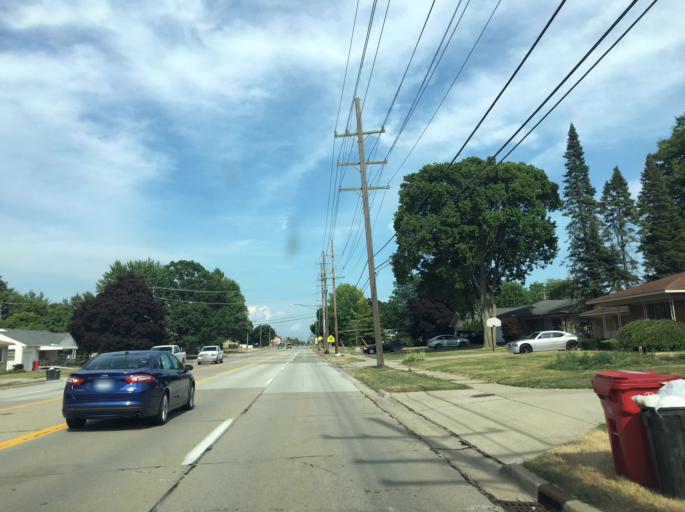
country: US
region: Michigan
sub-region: Macomb County
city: Fraser
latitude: 42.5387
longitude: -82.9581
